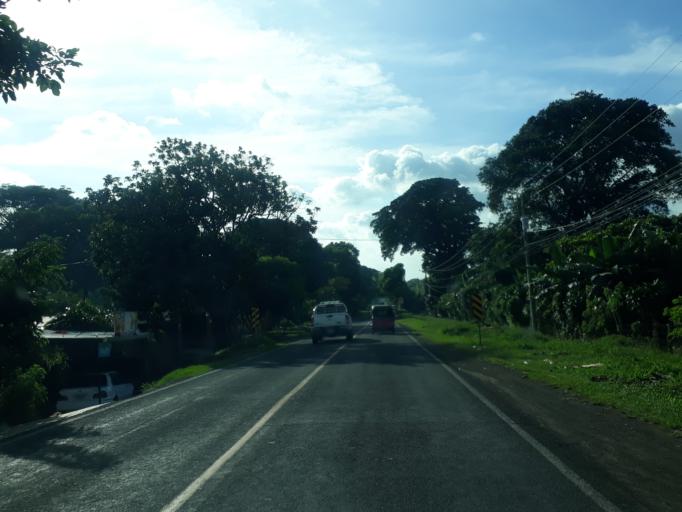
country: NI
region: Carazo
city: San Marcos
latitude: 11.9051
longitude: -86.1804
